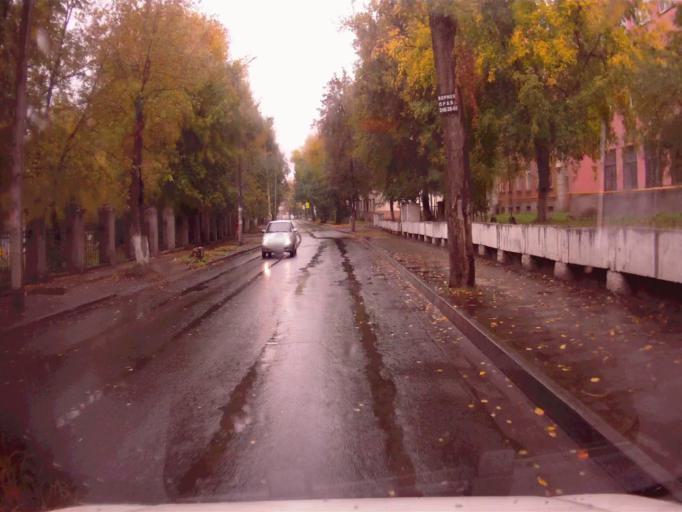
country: RU
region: Chelyabinsk
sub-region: Gorod Chelyabinsk
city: Chelyabinsk
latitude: 55.1919
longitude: 61.4121
